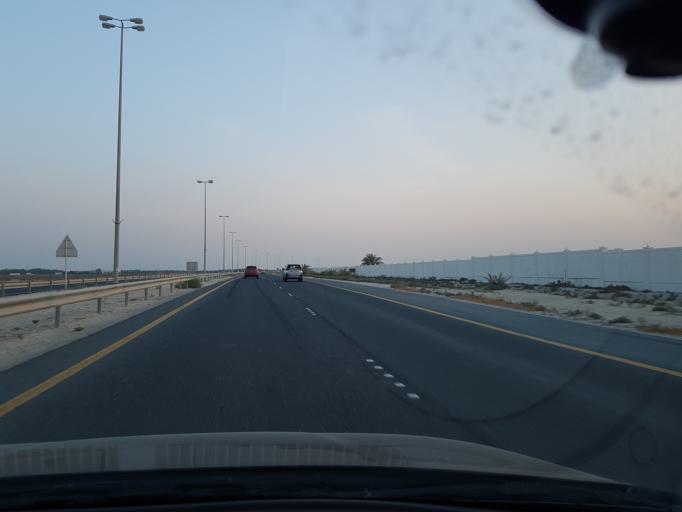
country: BH
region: Central Governorate
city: Dar Kulayb
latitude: 26.0366
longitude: 50.4998
